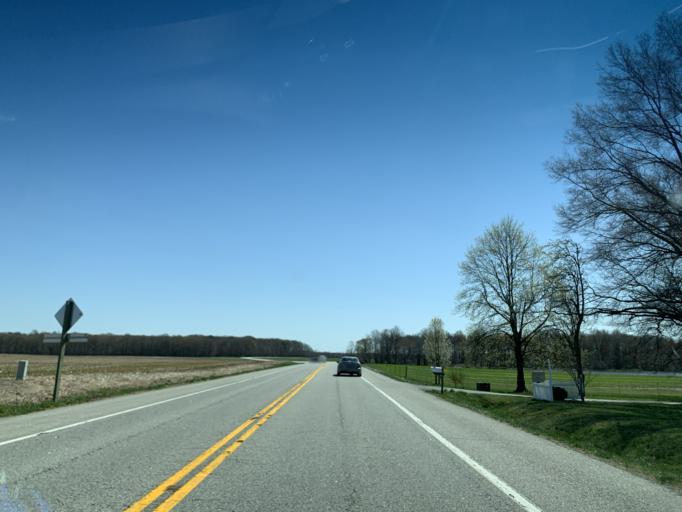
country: US
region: Maryland
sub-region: Queen Anne's County
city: Centreville
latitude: 38.9926
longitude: -76.0388
